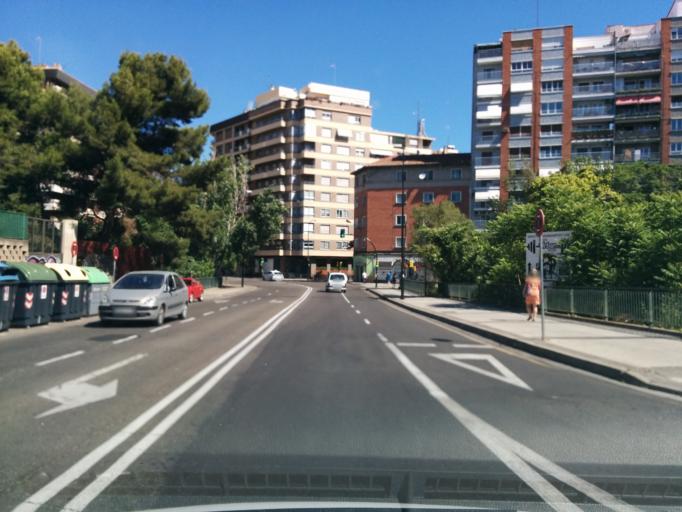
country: ES
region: Aragon
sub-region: Provincia de Zaragoza
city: Delicias
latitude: 41.6372
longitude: -0.8946
